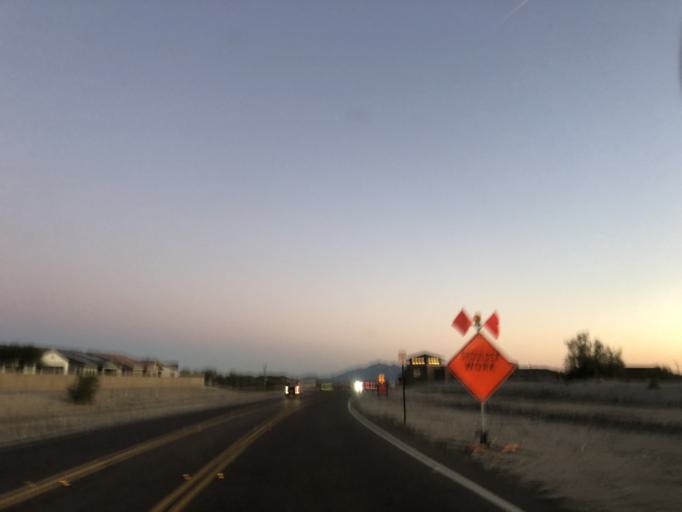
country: US
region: Arizona
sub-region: Maricopa County
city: Citrus Park
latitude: 33.5007
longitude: -112.5049
